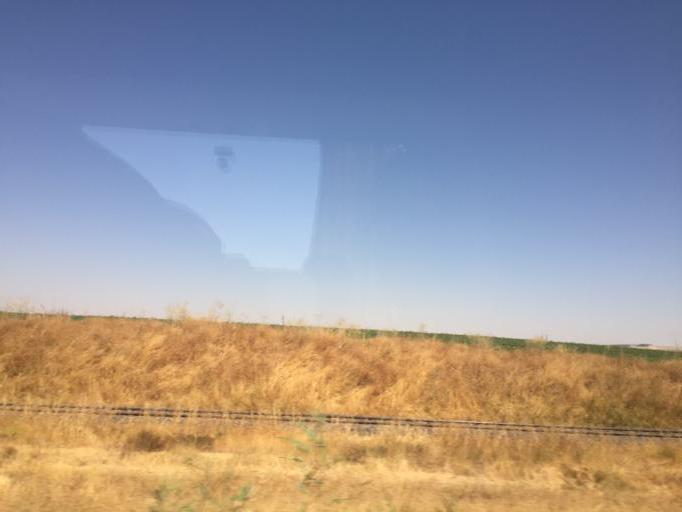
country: TR
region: Diyarbakir
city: Tepe
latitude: 37.8509
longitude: 40.7567
